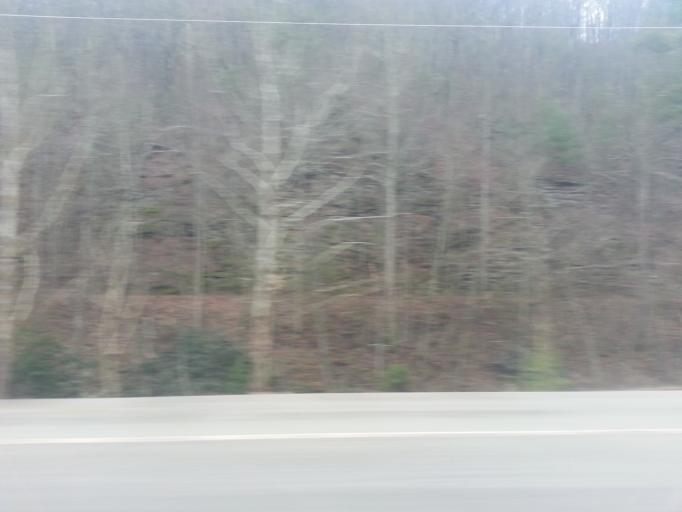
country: US
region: Tennessee
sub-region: Morgan County
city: Coalfield
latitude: 35.9853
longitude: -84.4821
